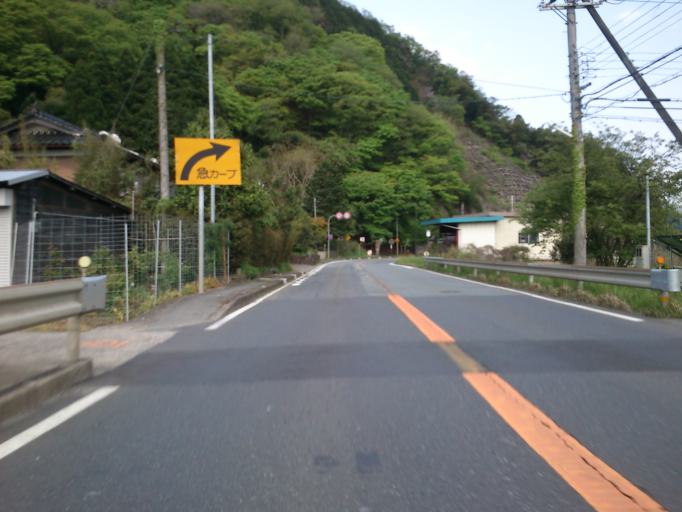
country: JP
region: Kyoto
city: Fukuchiyama
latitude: 35.3259
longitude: 134.9647
